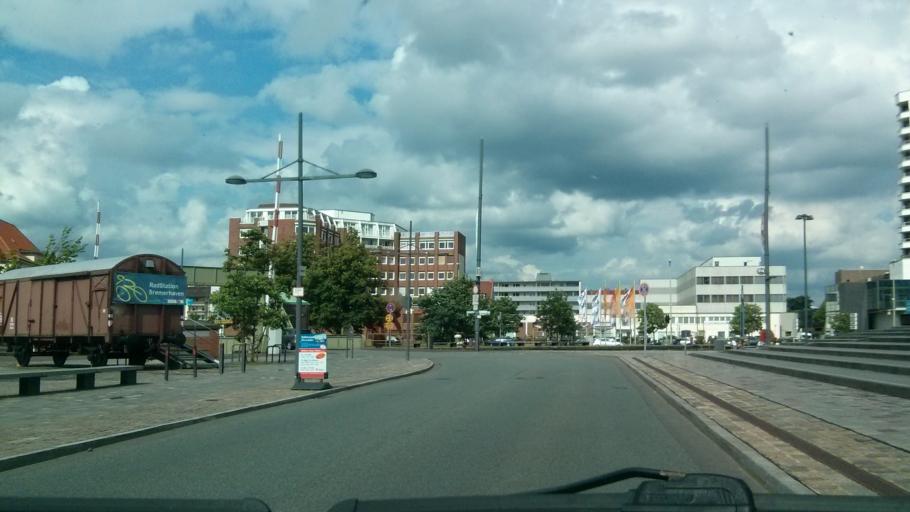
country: DE
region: Bremen
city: Bremerhaven
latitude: 53.5438
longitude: 8.5740
